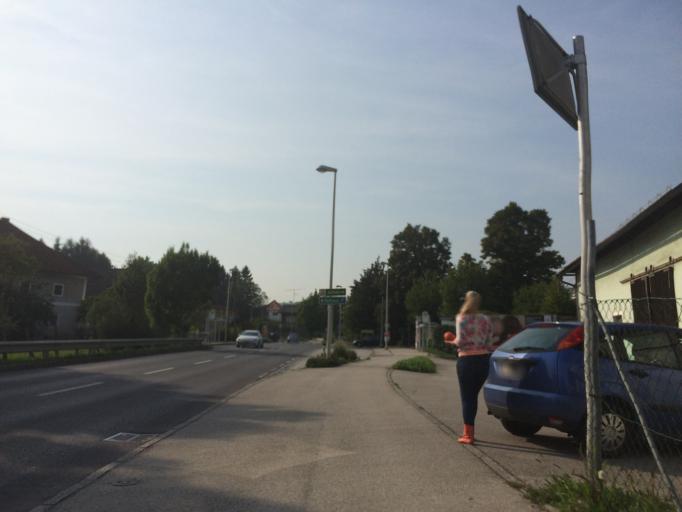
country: AT
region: Upper Austria
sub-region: Politischer Bezirk Linz-Land
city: Leonding
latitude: 48.2767
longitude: 14.2500
